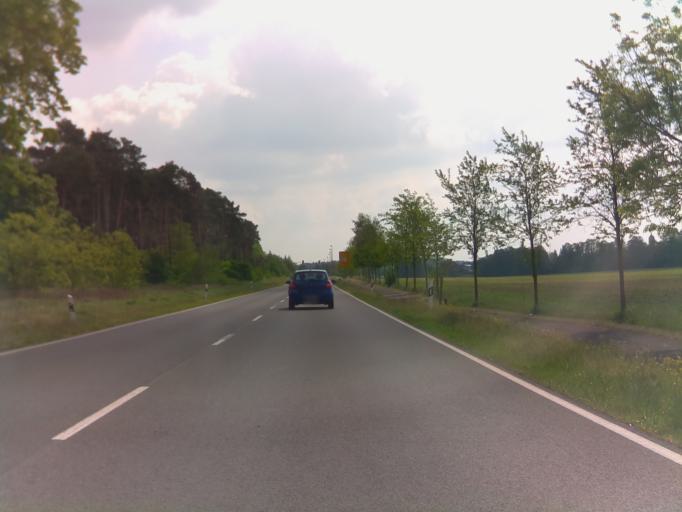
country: DE
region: Saxony-Anhalt
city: Gardelegen
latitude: 52.5287
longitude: 11.4435
